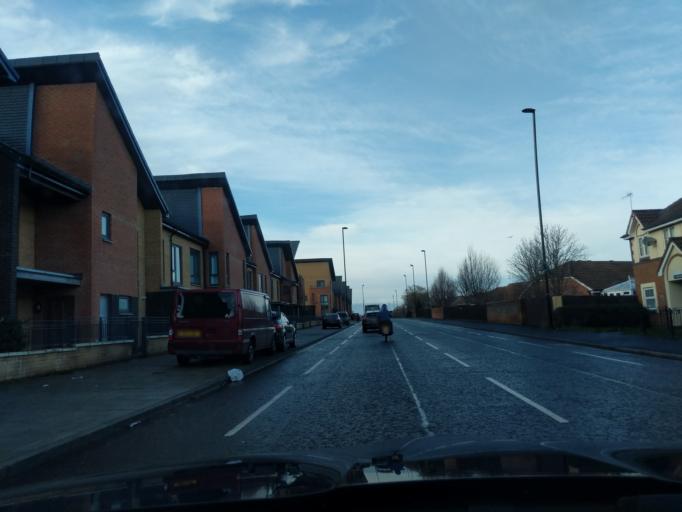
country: GB
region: England
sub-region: Gateshead
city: Felling
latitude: 54.9658
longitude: -1.5626
